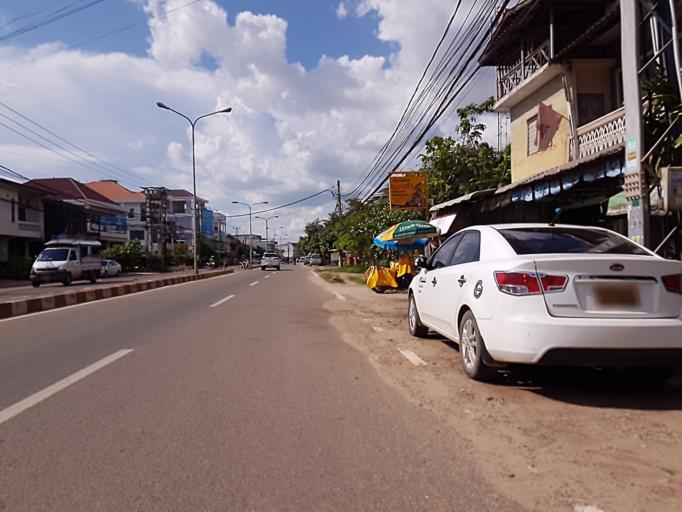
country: TH
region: Nong Khai
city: Si Chiang Mai
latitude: 17.9237
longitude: 102.6174
